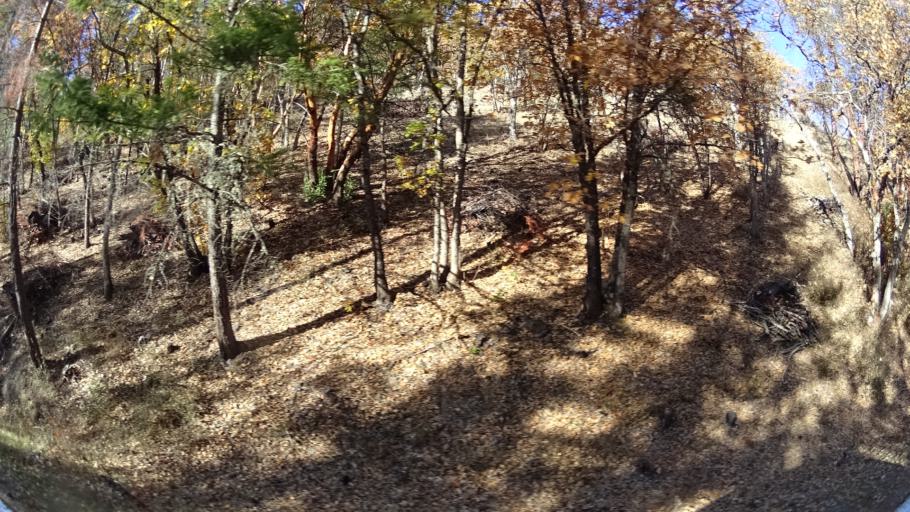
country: US
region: California
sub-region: Siskiyou County
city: Yreka
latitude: 41.8977
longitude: -122.8262
